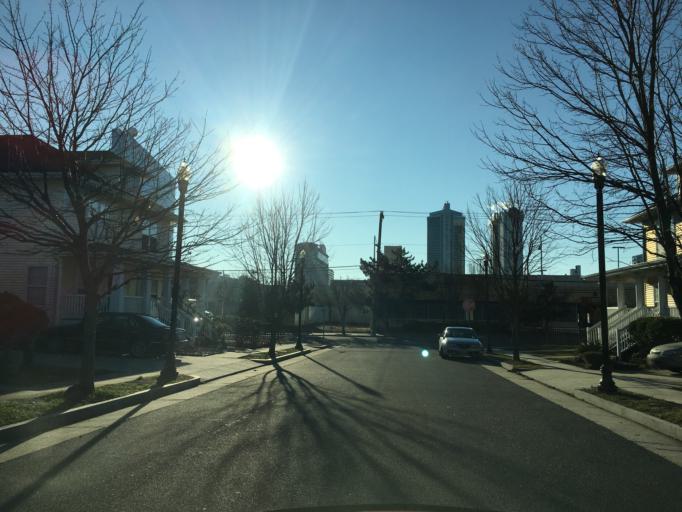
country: US
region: New Jersey
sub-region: Atlantic County
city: Atlantic City
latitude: 39.3669
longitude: -74.4223
